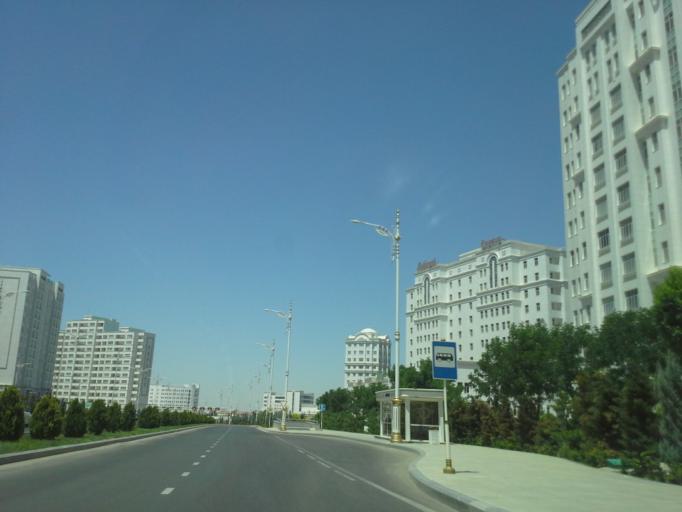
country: TM
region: Ahal
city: Ashgabat
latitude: 37.9348
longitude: 58.3668
